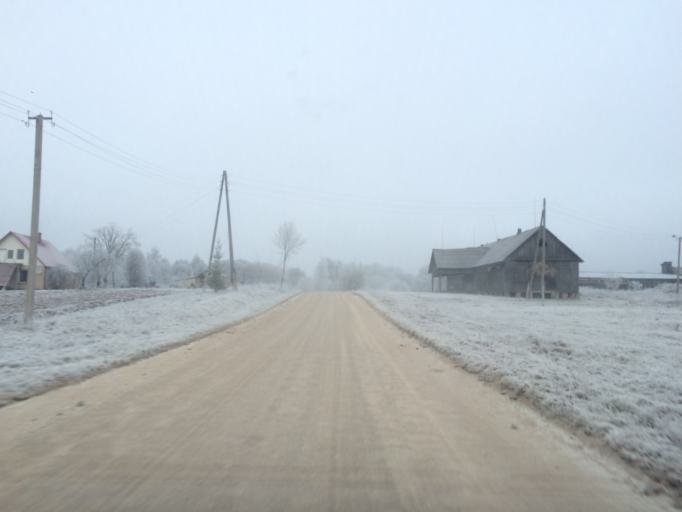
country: LV
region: Ludzas Rajons
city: Ludza
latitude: 56.6221
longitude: 27.5181
